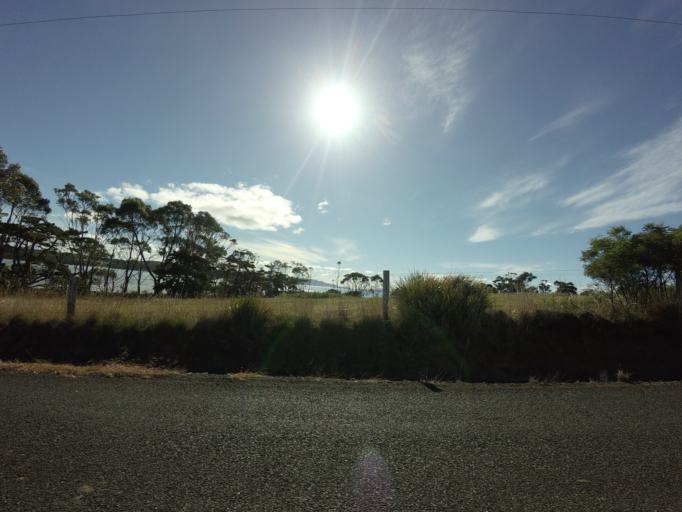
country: AU
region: Tasmania
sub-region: Clarence
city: Sandford
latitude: -43.0120
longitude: 147.7138
